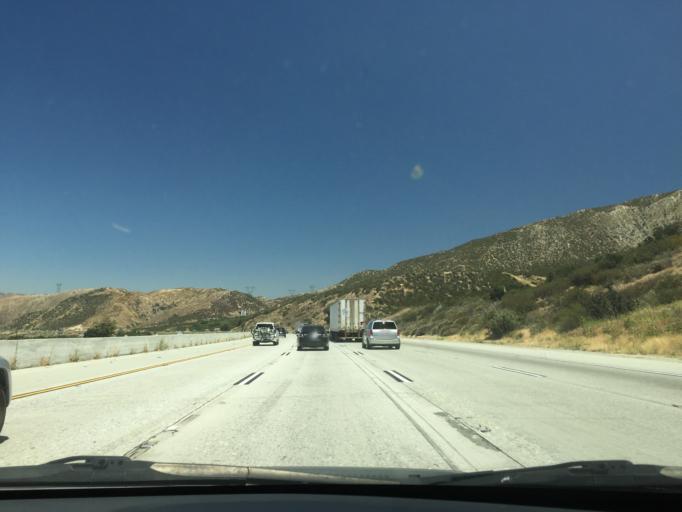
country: US
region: California
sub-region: San Bernardino County
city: Oak Hills
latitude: 34.2878
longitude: -117.4515
